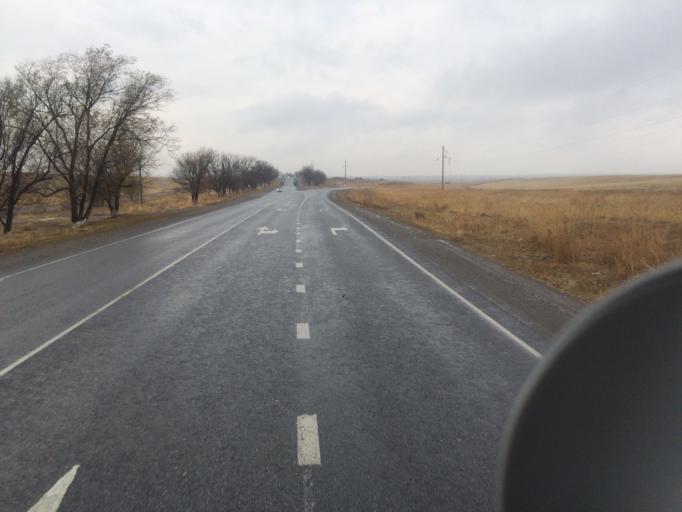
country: KZ
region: Zhambyl
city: Georgiyevka
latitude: 43.0389
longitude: 74.7667
